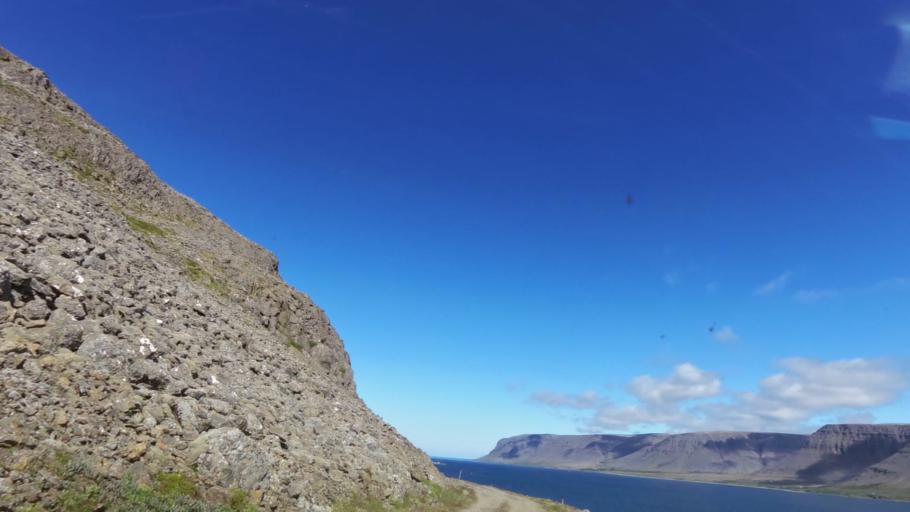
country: IS
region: West
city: Olafsvik
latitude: 65.6232
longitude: -23.8851
